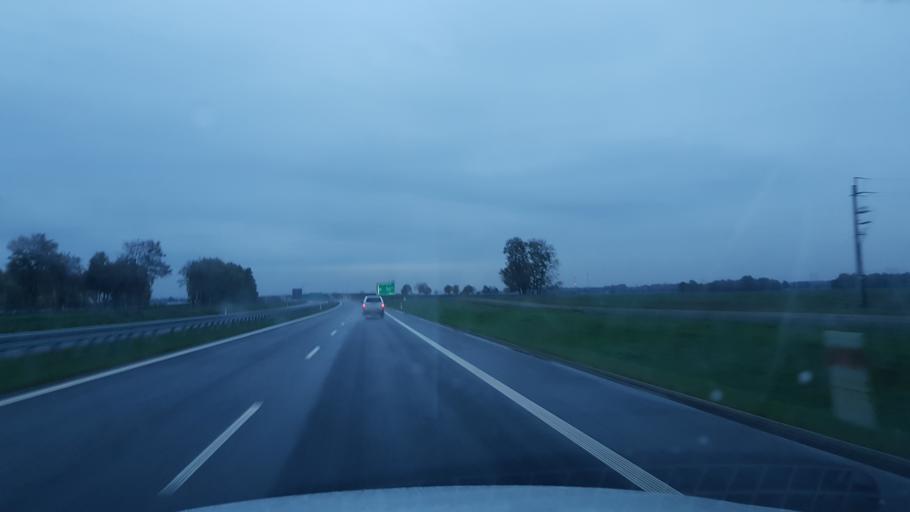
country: PL
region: West Pomeranian Voivodeship
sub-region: Powiat gryficki
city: Brojce
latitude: 53.8698
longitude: 15.3645
